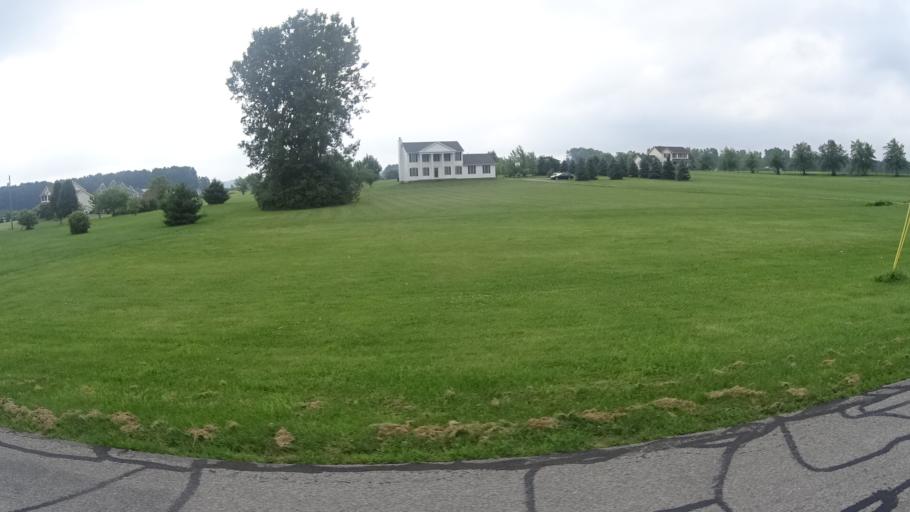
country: US
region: Ohio
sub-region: Erie County
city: Milan
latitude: 41.3070
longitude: -82.5091
